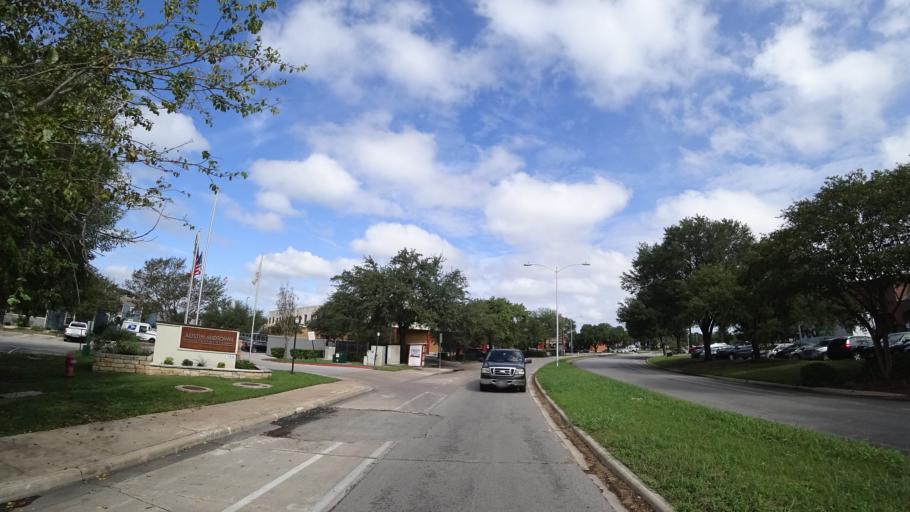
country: US
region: Texas
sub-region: Travis County
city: West Lake Hills
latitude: 30.3560
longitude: -97.7367
